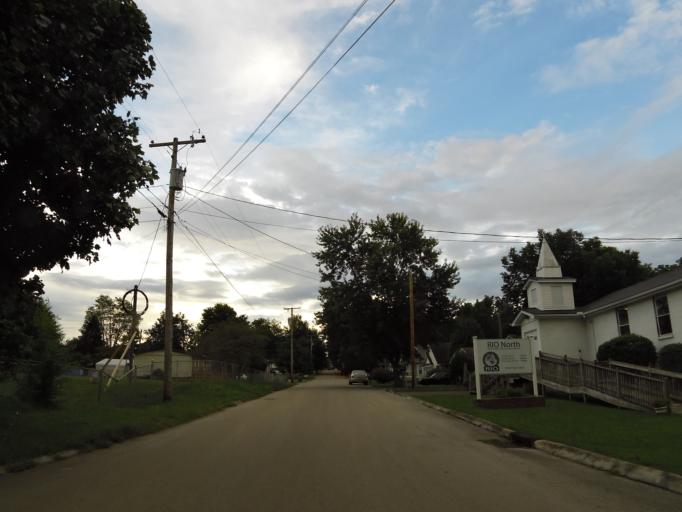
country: US
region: Tennessee
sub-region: Blount County
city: Maryville
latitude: 35.7627
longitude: -83.9542
